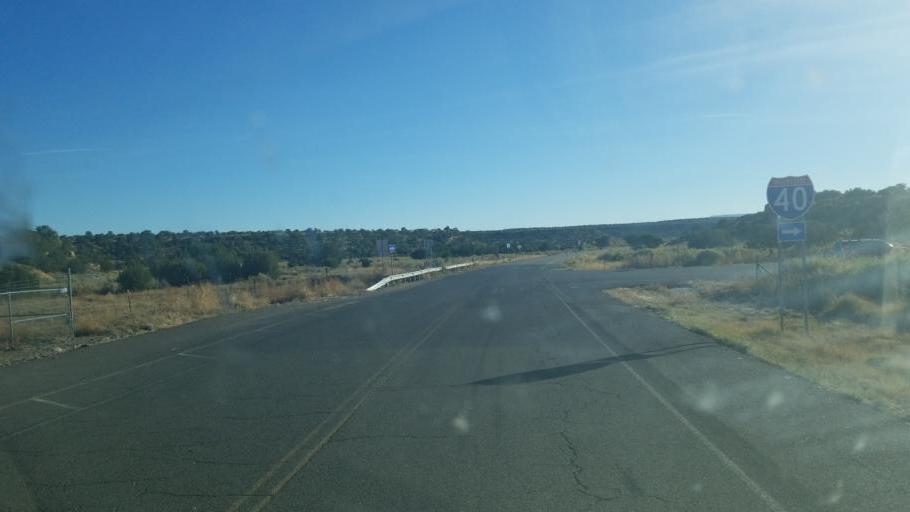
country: US
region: New Mexico
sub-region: Cibola County
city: Skyline-Ganipa
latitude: 35.0721
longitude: -107.5564
